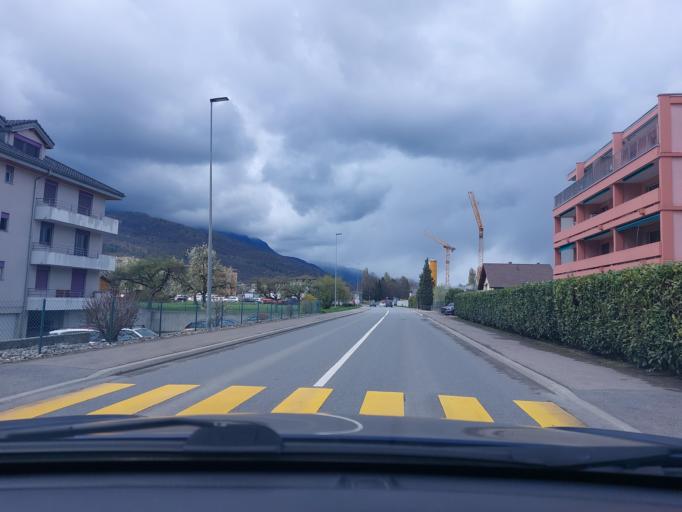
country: CH
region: Valais
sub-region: Monthey District
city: Monthey
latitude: 46.2583
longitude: 6.9591
